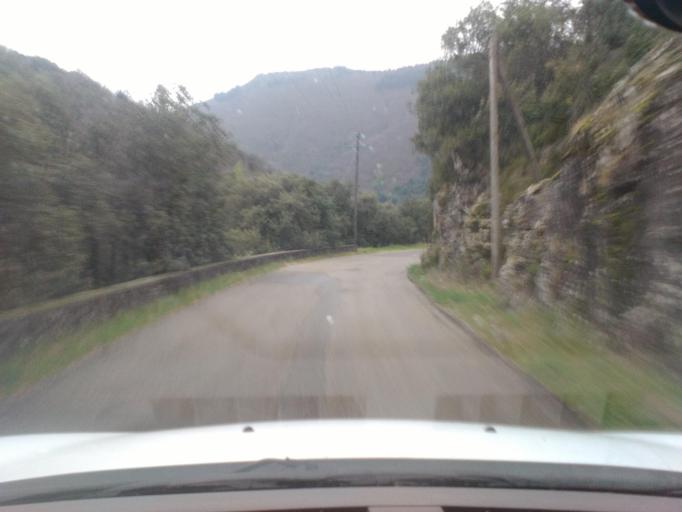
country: FR
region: Languedoc-Roussillon
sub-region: Departement du Gard
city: Valleraugue
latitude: 44.1052
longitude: 3.6346
